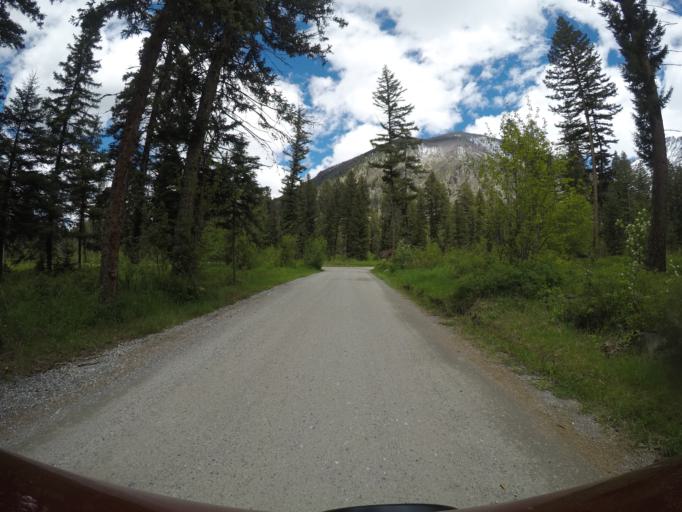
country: US
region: Montana
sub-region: Park County
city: Livingston
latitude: 45.4983
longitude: -110.5240
